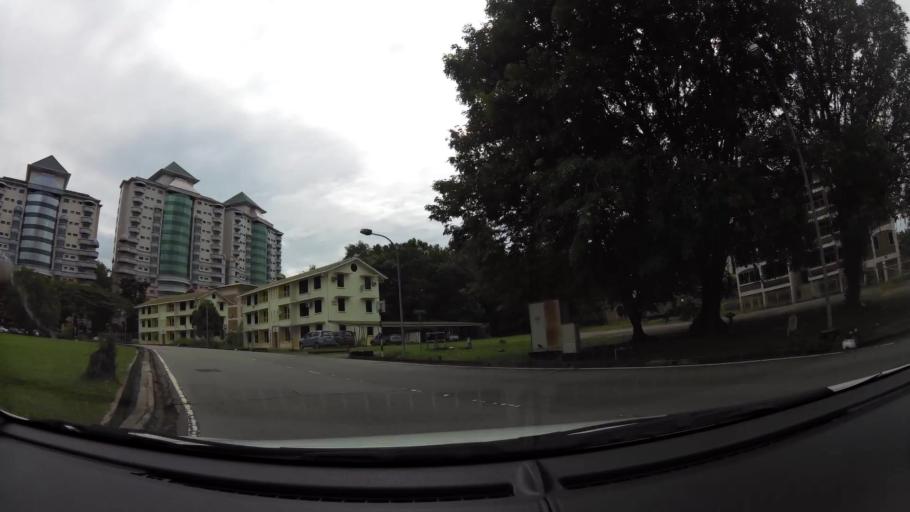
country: BN
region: Brunei and Muara
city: Bandar Seri Begawan
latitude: 4.9049
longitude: 114.9365
